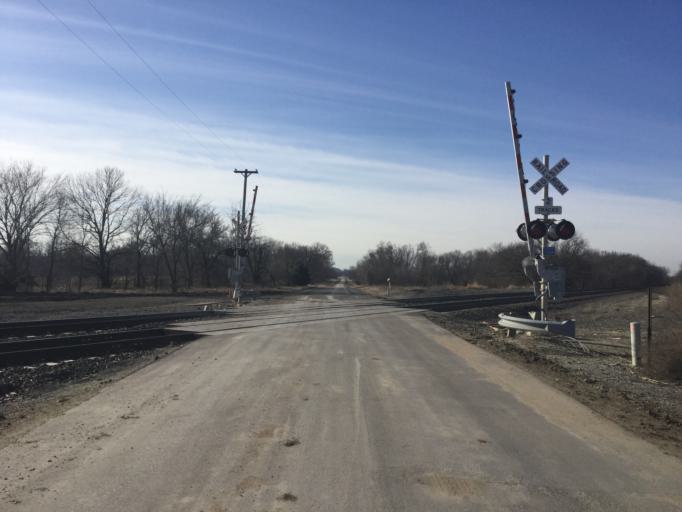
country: US
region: Kansas
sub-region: Osage County
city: Lyndon
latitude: 38.5694
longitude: -95.5272
